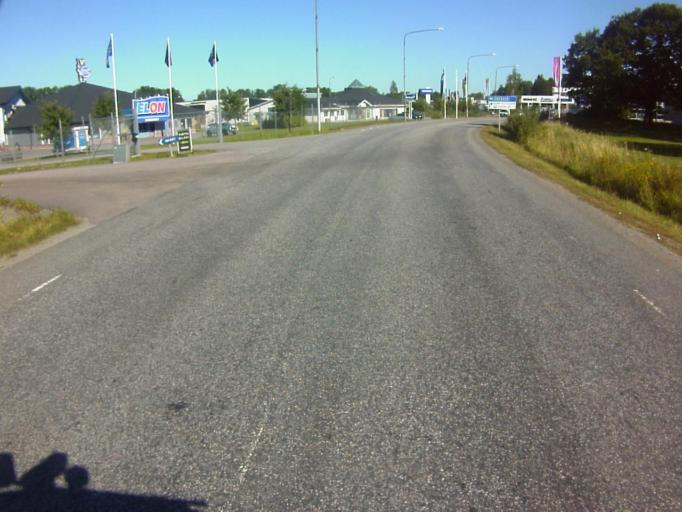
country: SE
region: Soedermanland
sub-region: Eskilstuna Kommun
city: Torshalla
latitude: 59.3861
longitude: 16.4681
